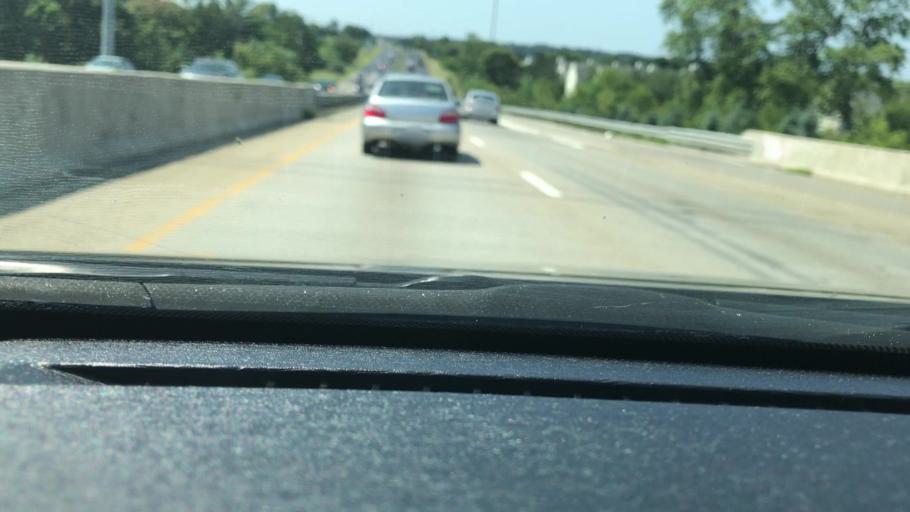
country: US
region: Massachusetts
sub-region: Essex County
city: Danvers
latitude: 42.5571
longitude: -70.9302
